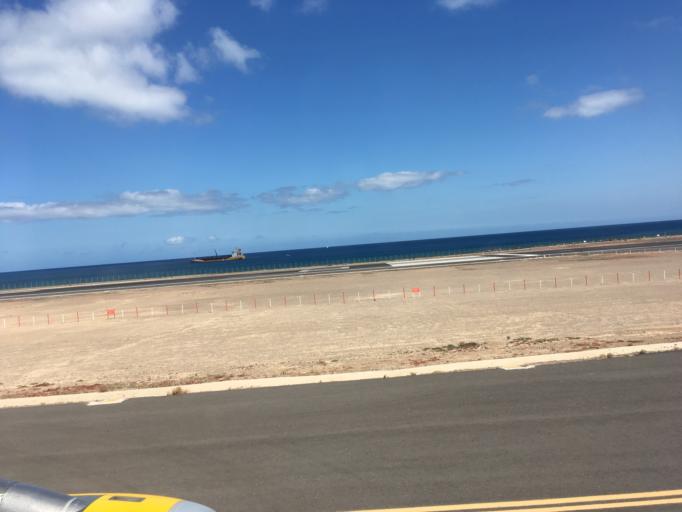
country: ES
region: Canary Islands
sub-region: Provincia de Las Palmas
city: Tias
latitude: 28.9377
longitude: -13.6118
